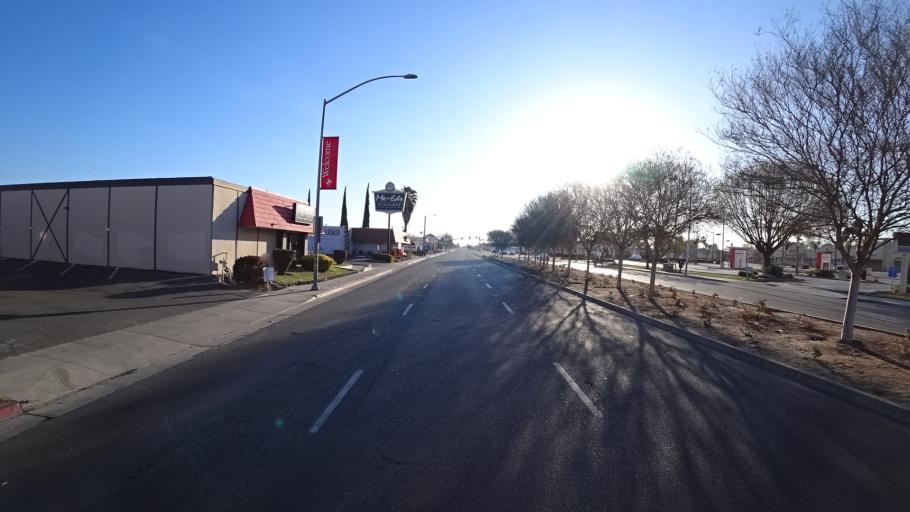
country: US
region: California
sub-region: Fresno County
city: Clovis
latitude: 36.8085
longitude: -119.7202
